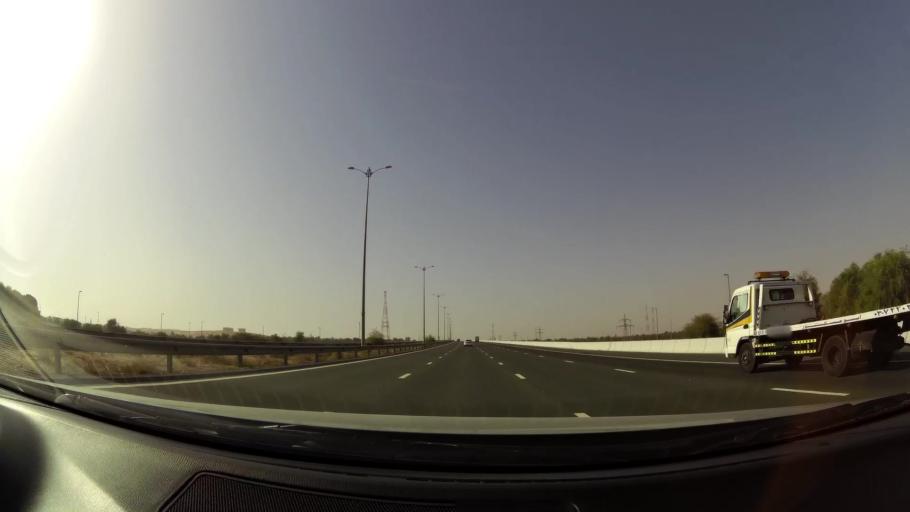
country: OM
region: Al Buraimi
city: Al Buraymi
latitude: 24.5864
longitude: 55.7401
